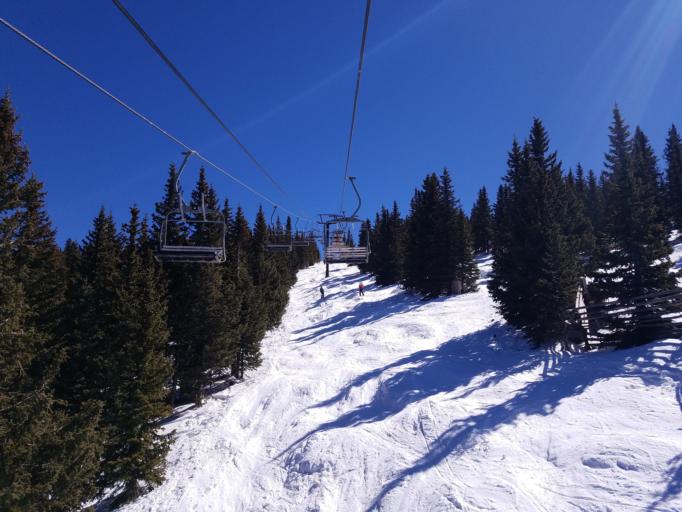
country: US
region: New Mexico
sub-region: Santa Fe County
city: Santa Fe
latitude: 35.7883
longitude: -105.7845
